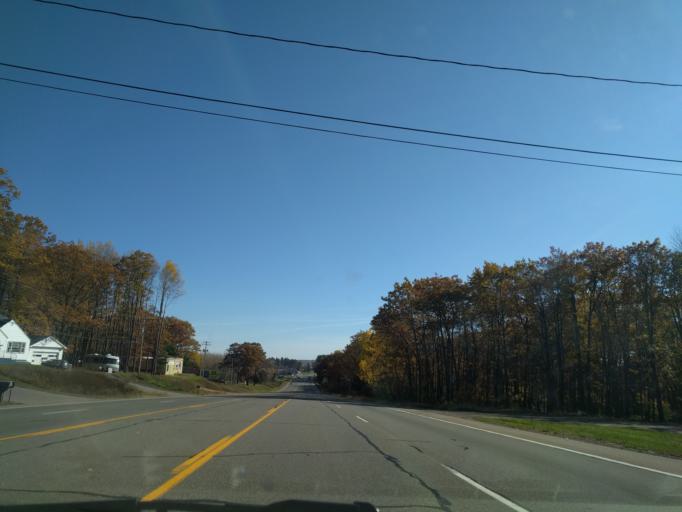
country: US
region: Michigan
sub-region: Dickinson County
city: Iron Mountain
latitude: 45.8569
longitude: -88.0584
